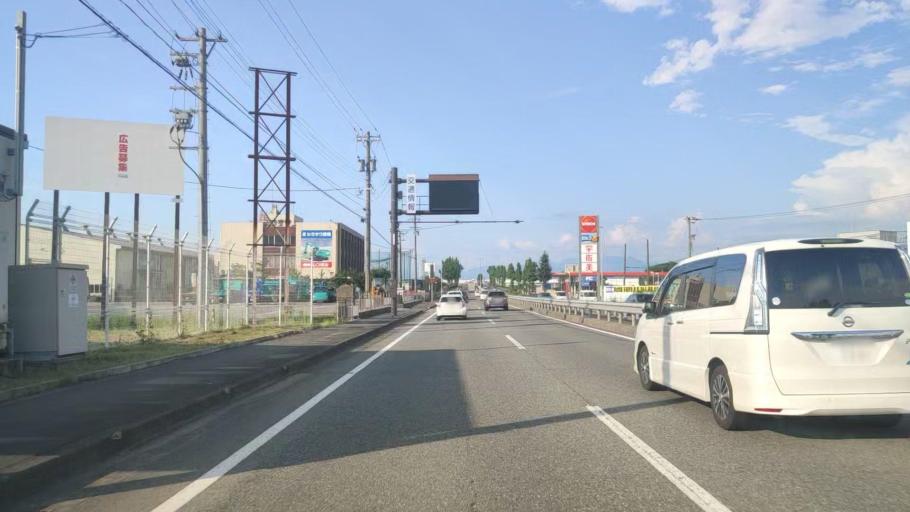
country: JP
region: Fukui
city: Fukui-shi
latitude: 36.0213
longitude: 136.2147
